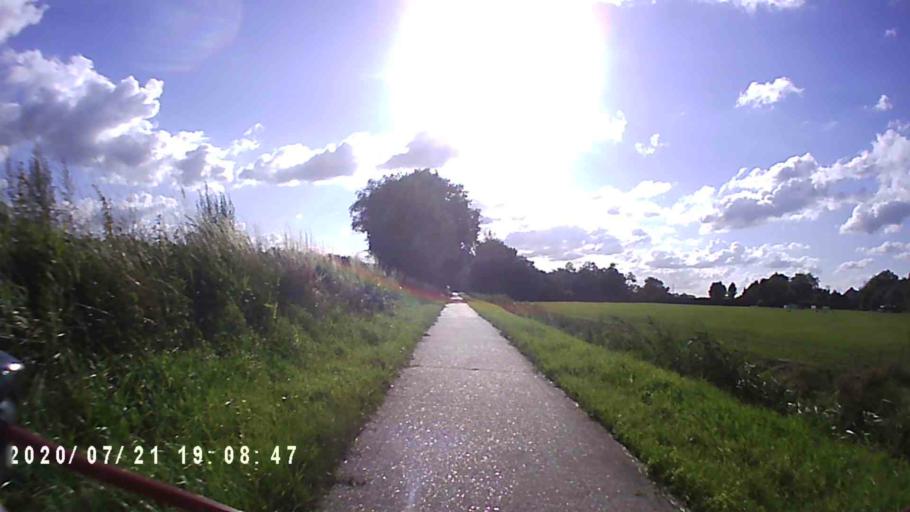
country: NL
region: Groningen
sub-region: Gemeente Hoogezand-Sappemeer
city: Hoogezand
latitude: 53.2347
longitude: 6.7169
